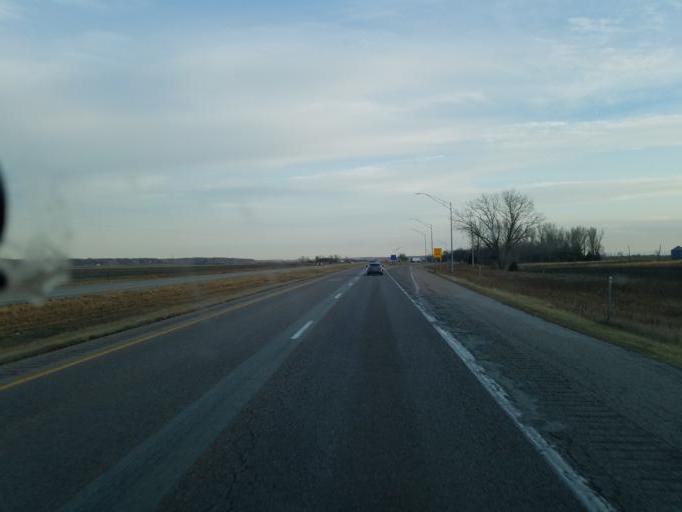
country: US
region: Iowa
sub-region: Harrison County
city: Missouri Valley
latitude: 41.5952
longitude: -95.9566
